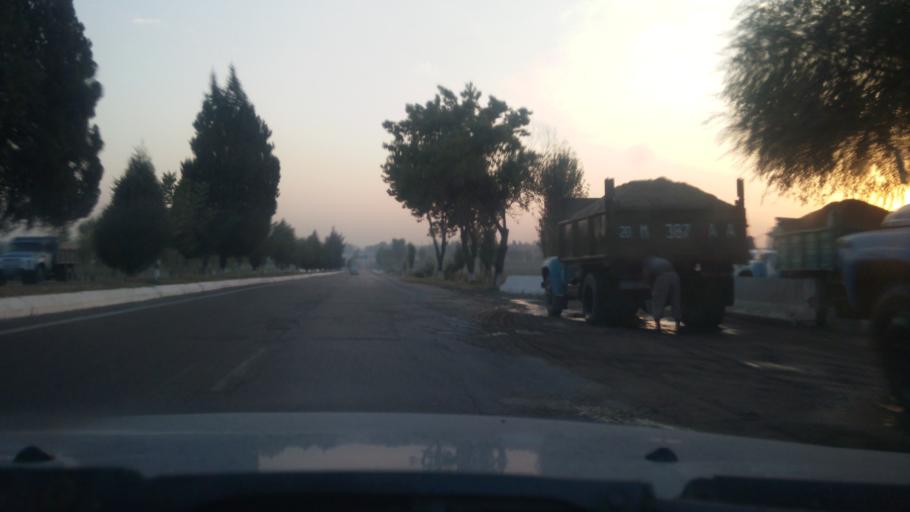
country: UZ
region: Toshkent
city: Amir Timur
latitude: 41.0459
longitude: 68.8889
